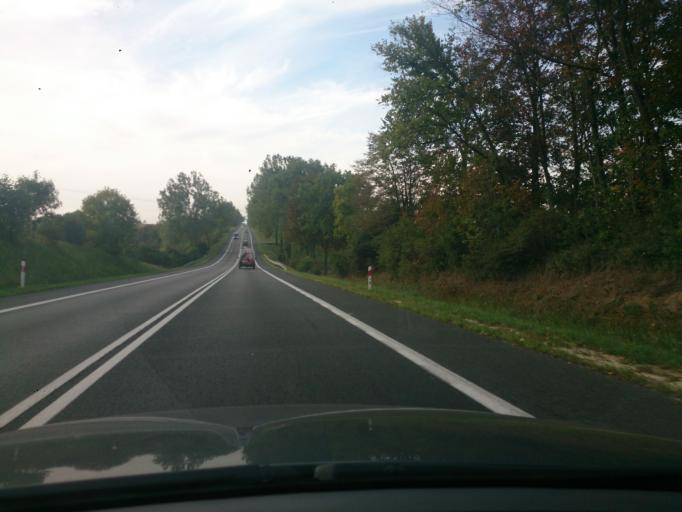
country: PL
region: Kujawsko-Pomorskie
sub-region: Powiat swiecki
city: Pruszcz
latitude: 53.3377
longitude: 18.2937
